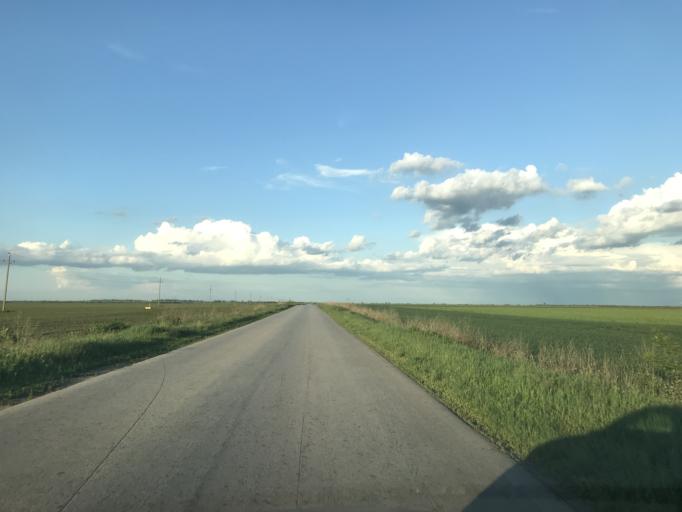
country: RS
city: Mihajlovo
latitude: 45.4488
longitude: 20.3989
